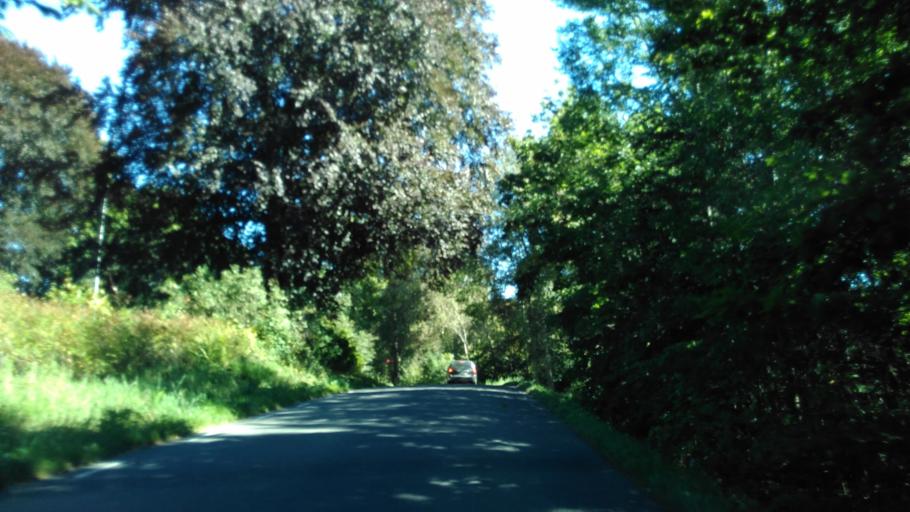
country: SE
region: Vaestra Goetaland
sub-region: Skara Kommun
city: Axvall
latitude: 58.4608
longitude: 13.6772
